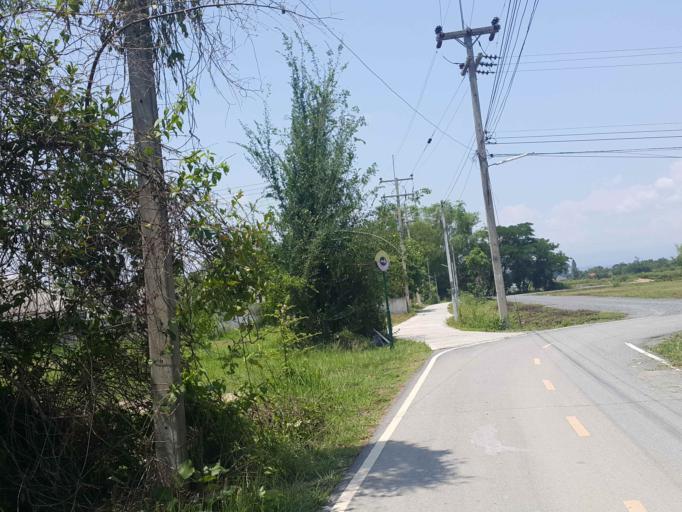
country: TH
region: Chiang Mai
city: San Sai
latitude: 18.8161
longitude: 99.0769
